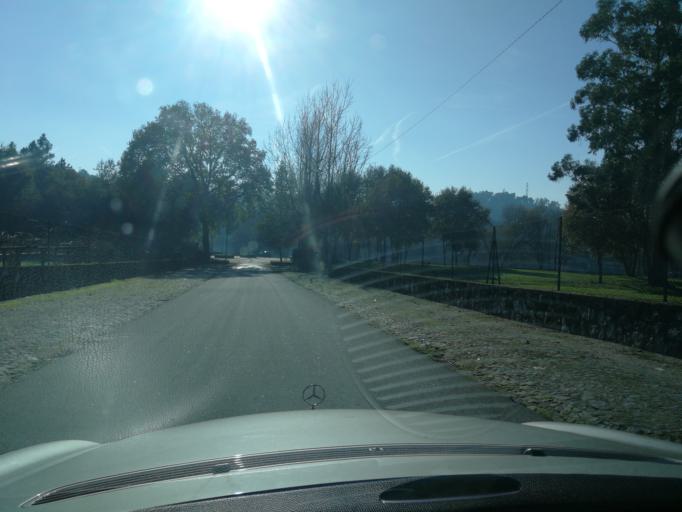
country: PT
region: Braga
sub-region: Braga
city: Adaufe
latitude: 41.6085
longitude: -8.4003
